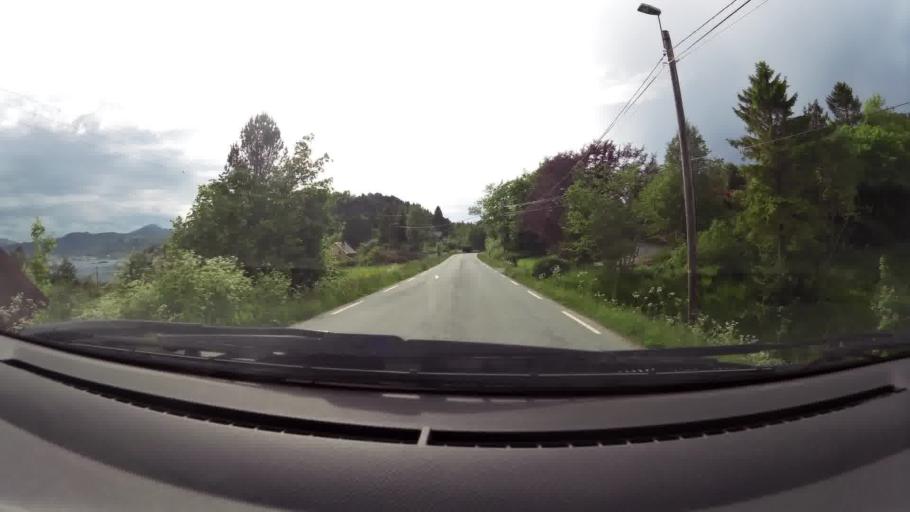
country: NO
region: More og Romsdal
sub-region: Kristiansund
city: Kristiansund
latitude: 63.0290
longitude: 7.7556
